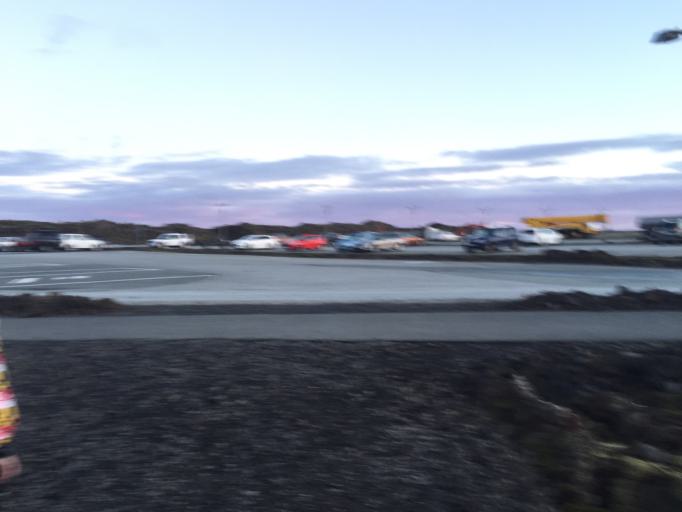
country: IS
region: Southern Peninsula
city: Grindavik
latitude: 63.8820
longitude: -22.4531
